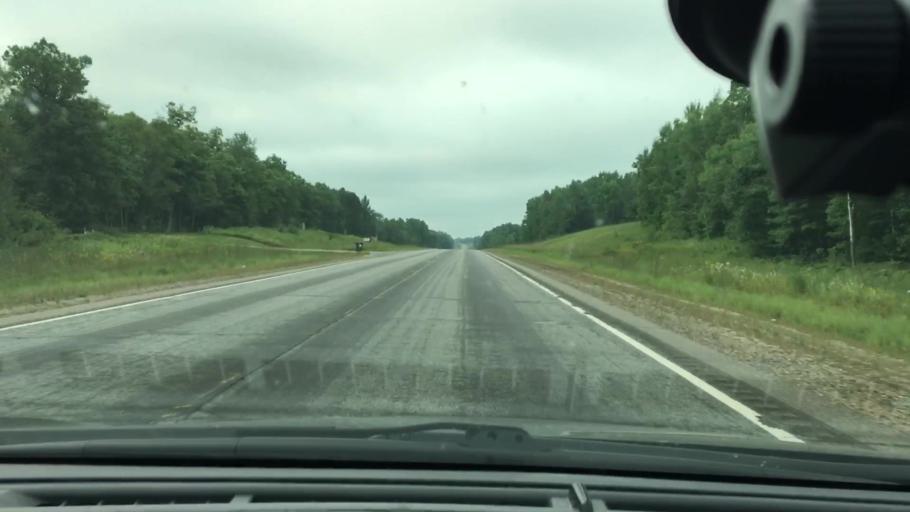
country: US
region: Minnesota
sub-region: Crow Wing County
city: Cross Lake
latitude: 46.7055
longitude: -93.9558
